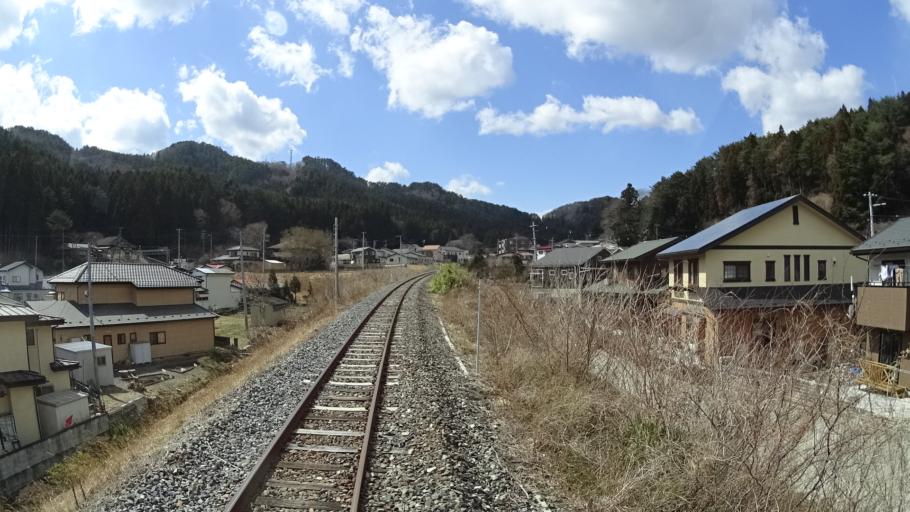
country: JP
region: Iwate
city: Otsuchi
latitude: 39.3675
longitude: 141.9360
